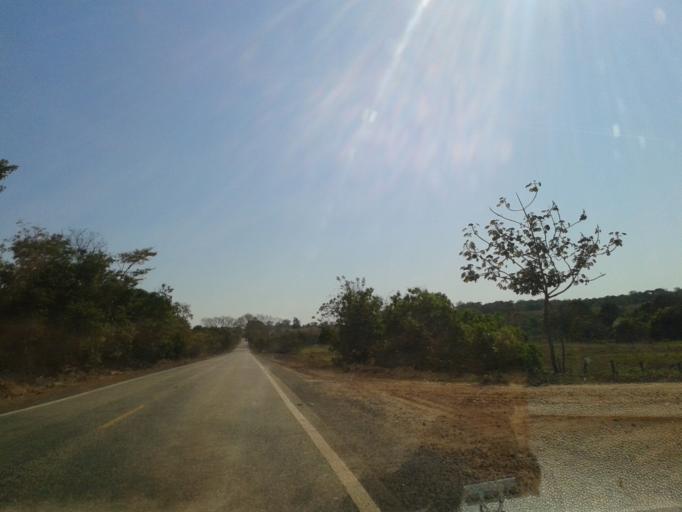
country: BR
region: Goias
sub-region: Mozarlandia
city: Mozarlandia
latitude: -14.5773
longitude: -50.5031
